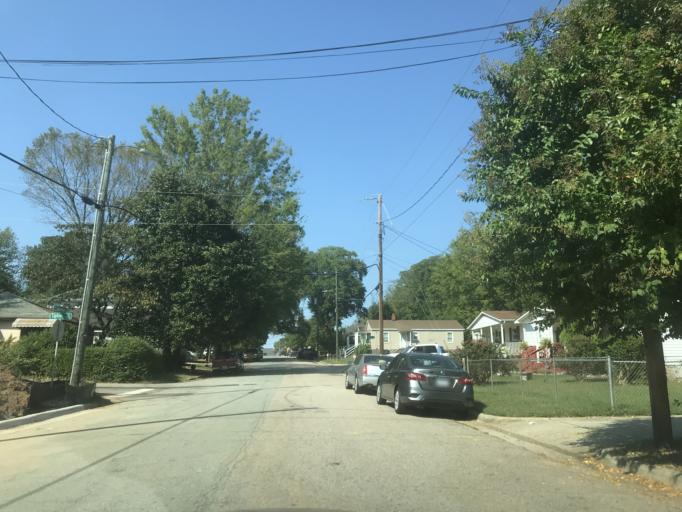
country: US
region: North Carolina
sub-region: Wake County
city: Raleigh
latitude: 35.7699
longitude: -78.6225
